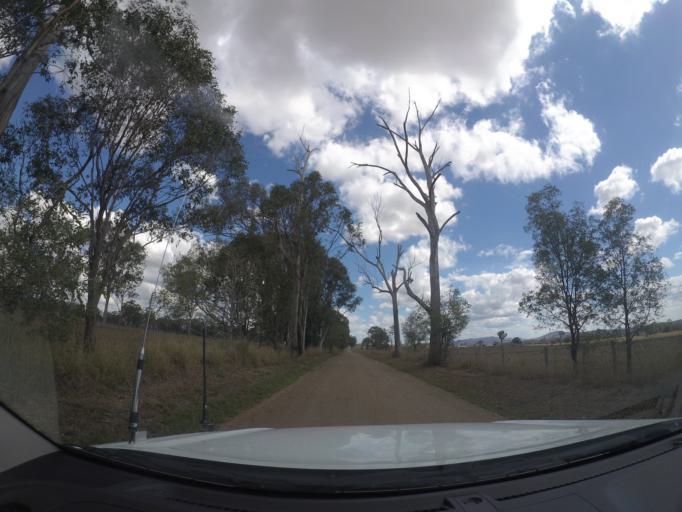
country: AU
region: Queensland
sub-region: Logan
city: Cedar Vale
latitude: -27.8885
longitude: 152.9600
